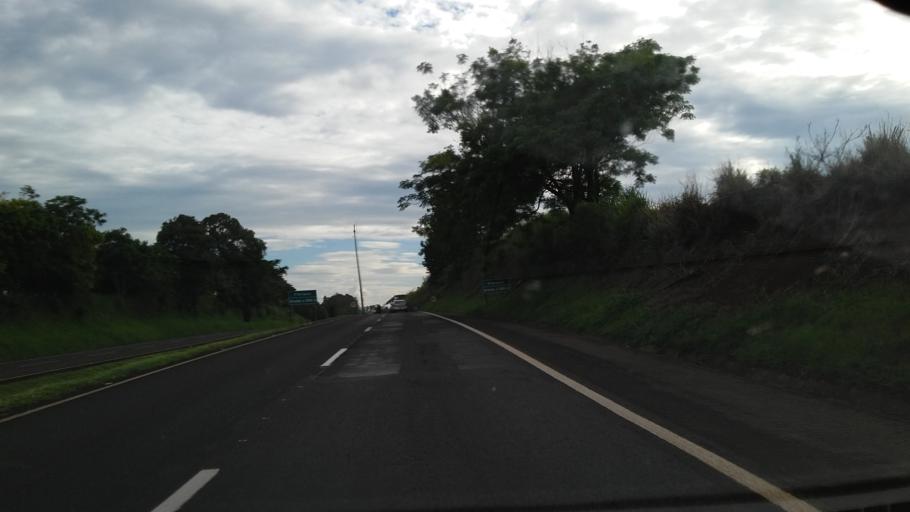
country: BR
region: Parana
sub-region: Paicandu
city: Paicandu
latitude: -23.5153
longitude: -52.0270
